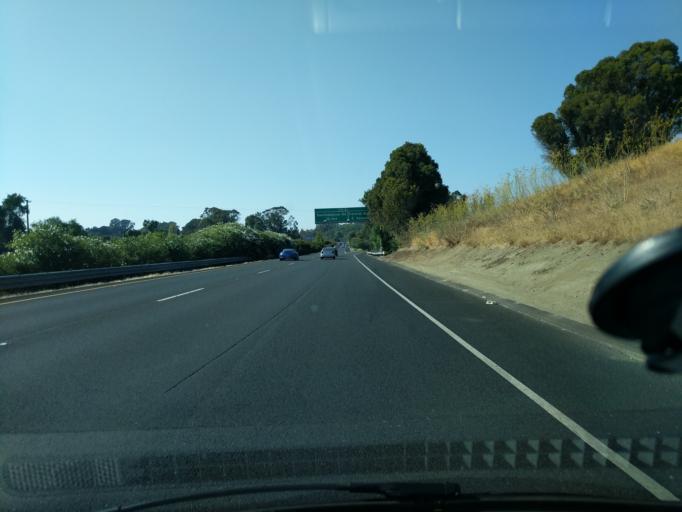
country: US
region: California
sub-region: Solano County
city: Benicia
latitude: 38.0557
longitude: -122.1475
